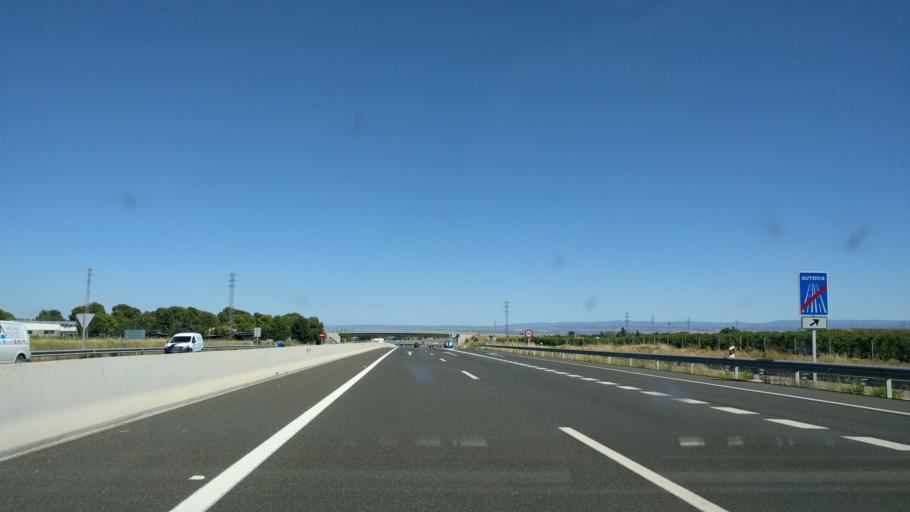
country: ES
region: Catalonia
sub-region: Provincia de Lleida
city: Alpicat
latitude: 41.6514
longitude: 0.5521
